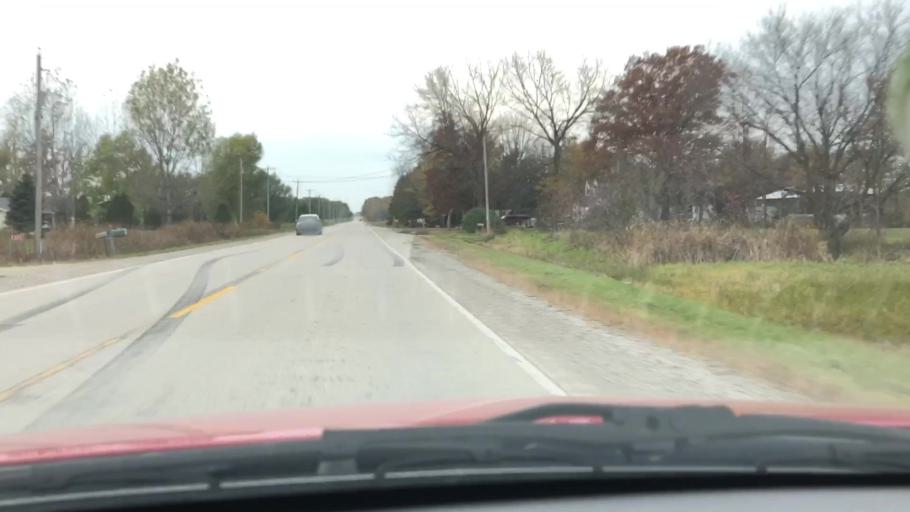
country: US
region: Wisconsin
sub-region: Brown County
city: Oneida
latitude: 44.4442
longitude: -88.2074
